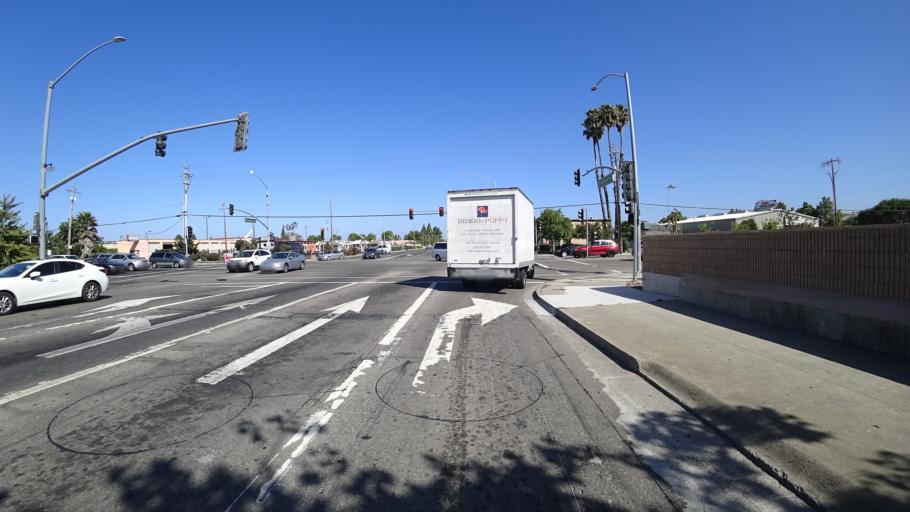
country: US
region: California
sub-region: Alameda County
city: Union City
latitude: 37.6215
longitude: -122.0566
